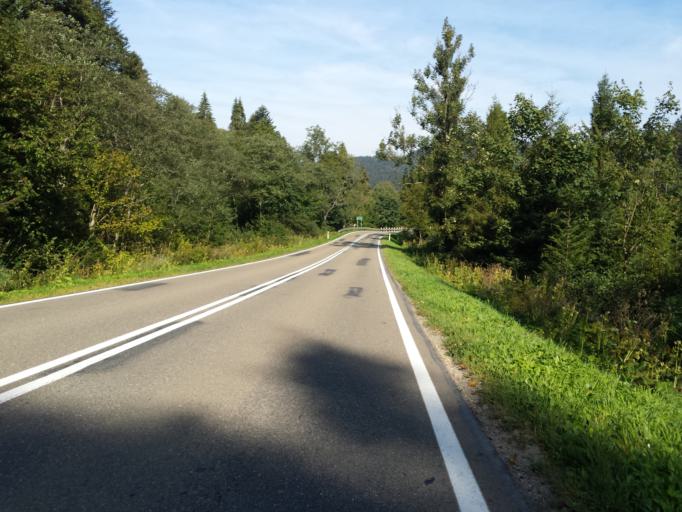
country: PL
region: Subcarpathian Voivodeship
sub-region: Powiat leski
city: Baligrod
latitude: 49.2856
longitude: 22.2750
